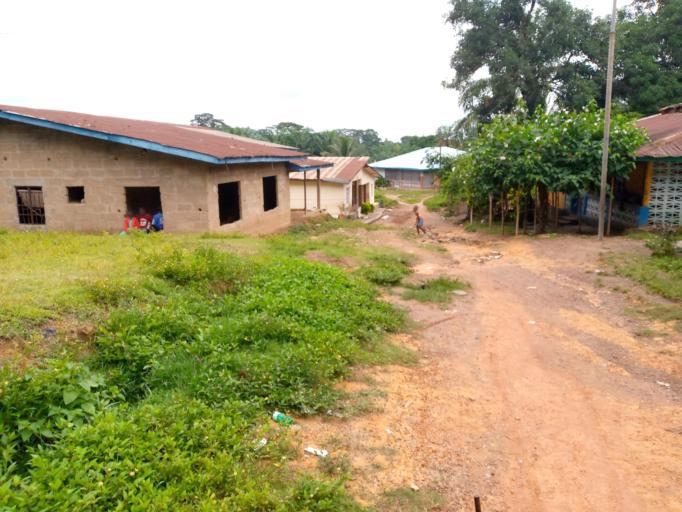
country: SL
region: Northern Province
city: Magburaka
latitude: 8.7259
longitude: -11.9497
